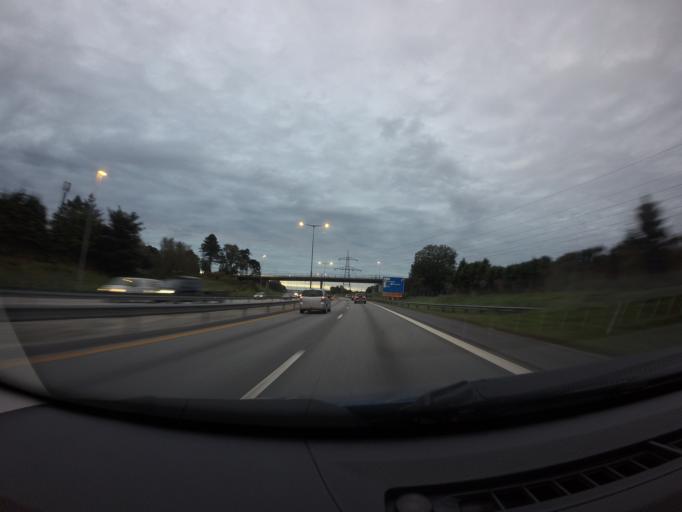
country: NO
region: Rogaland
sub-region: Sola
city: Sola
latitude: 58.9127
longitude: 5.6951
